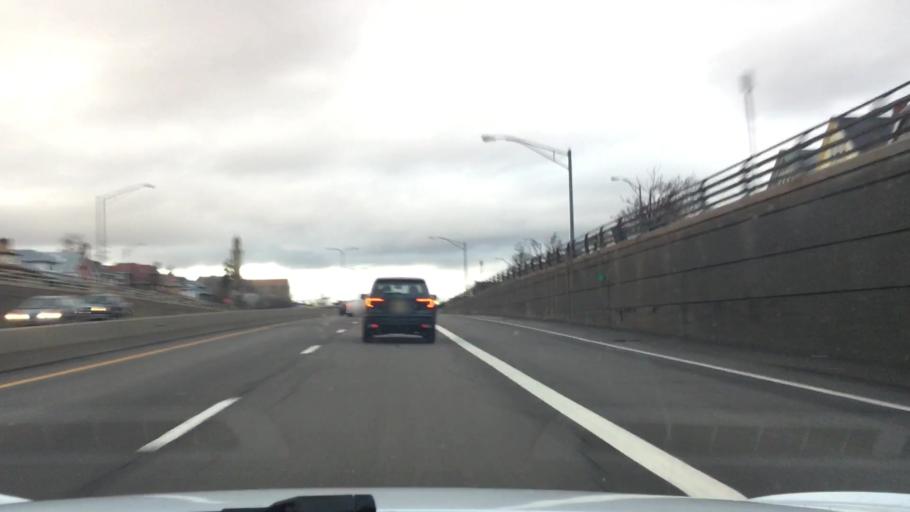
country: US
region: New York
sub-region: Erie County
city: Buffalo
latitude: 42.9157
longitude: -78.8433
